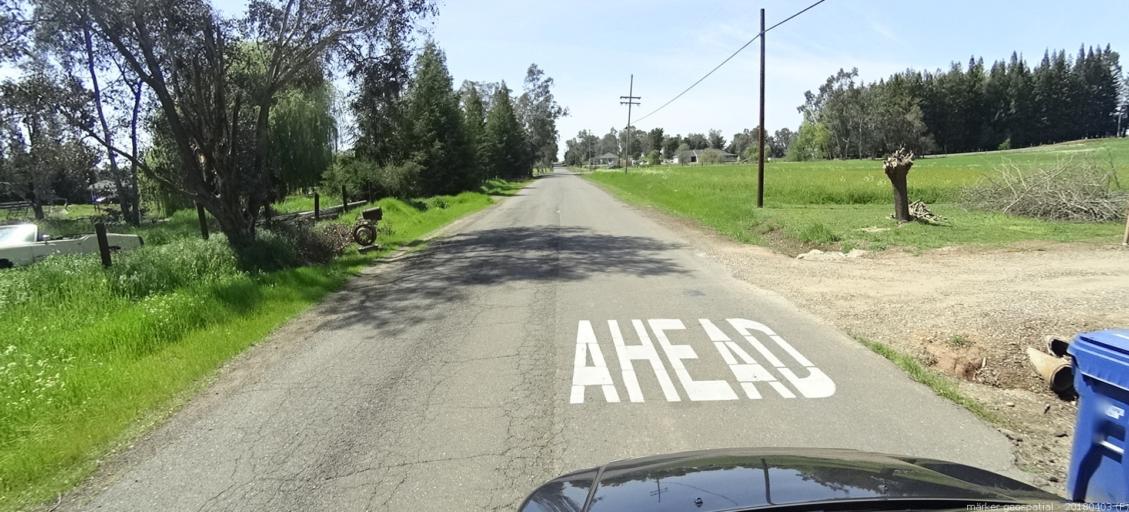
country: US
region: California
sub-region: Sacramento County
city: Herald
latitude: 38.3579
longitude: -121.2220
